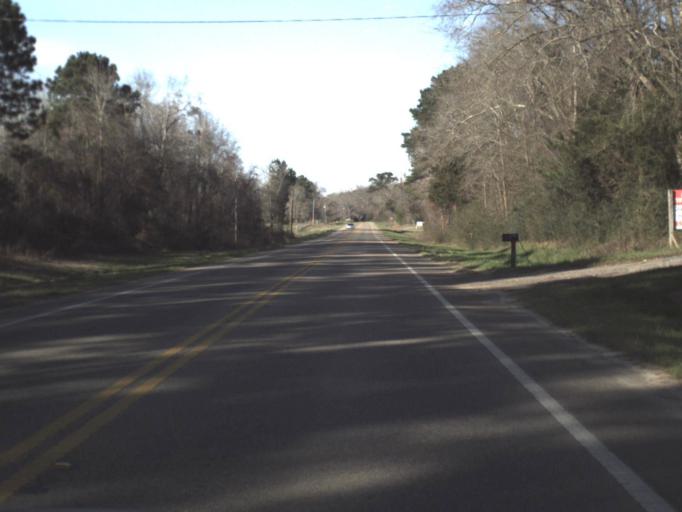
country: US
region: Florida
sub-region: Jackson County
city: Marianna
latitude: 30.7017
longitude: -85.2321
